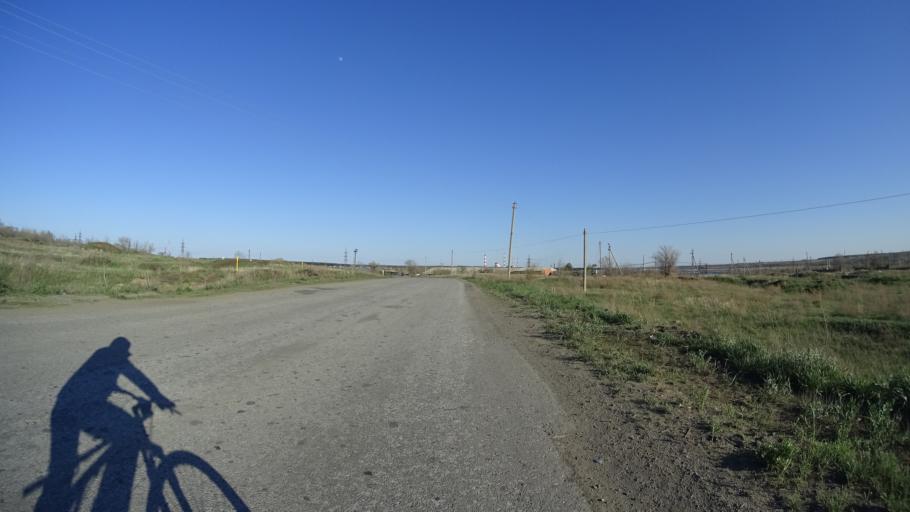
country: RU
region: Chelyabinsk
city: Troitsk
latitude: 54.0775
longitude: 61.6004
